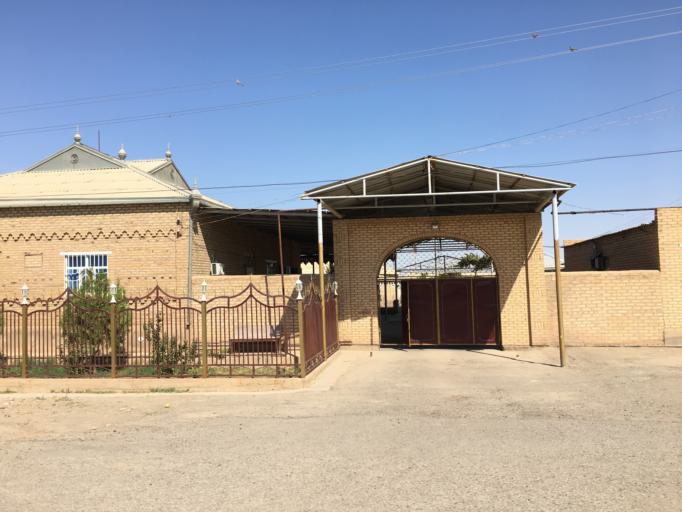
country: IR
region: Razavi Khorasan
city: Sarakhs
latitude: 36.5190
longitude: 61.2194
